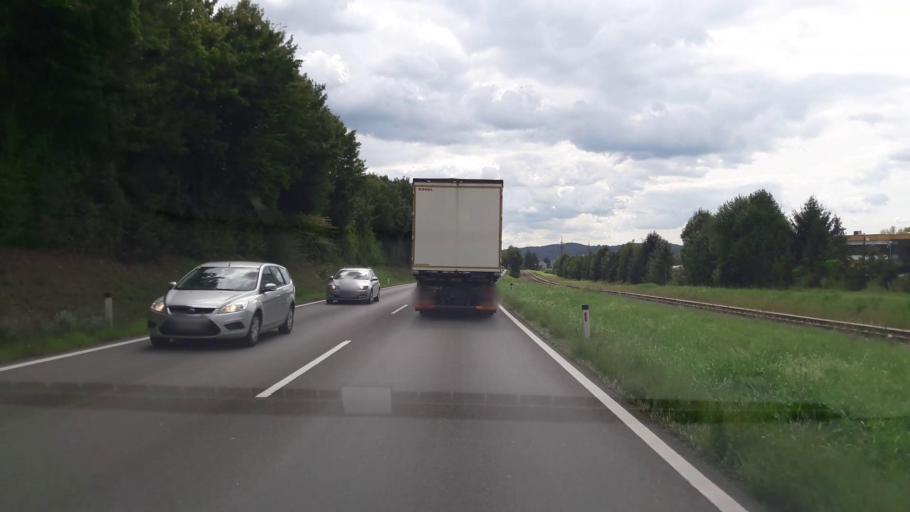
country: AT
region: Styria
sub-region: Politischer Bezirk Weiz
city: Gleisdorf
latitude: 47.1187
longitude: 15.6998
